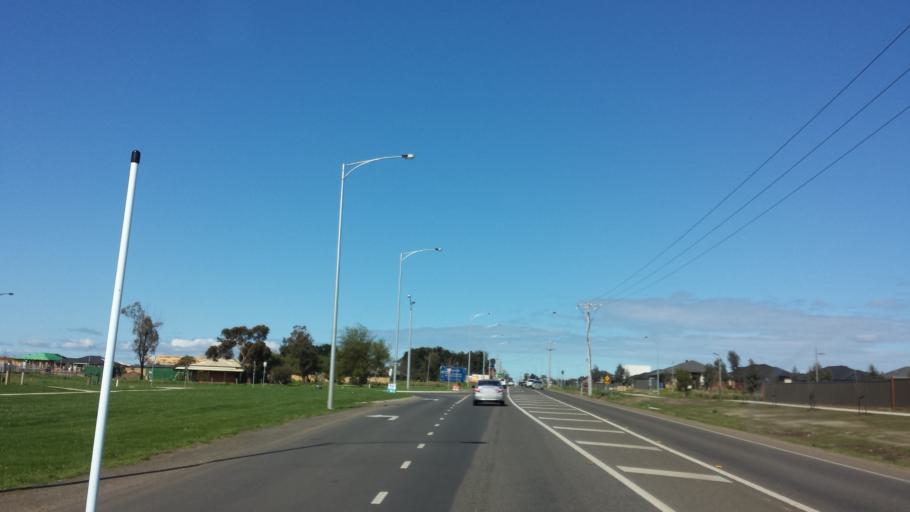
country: AU
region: Victoria
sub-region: Casey
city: Cranbourne East
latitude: -38.1063
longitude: 145.3298
